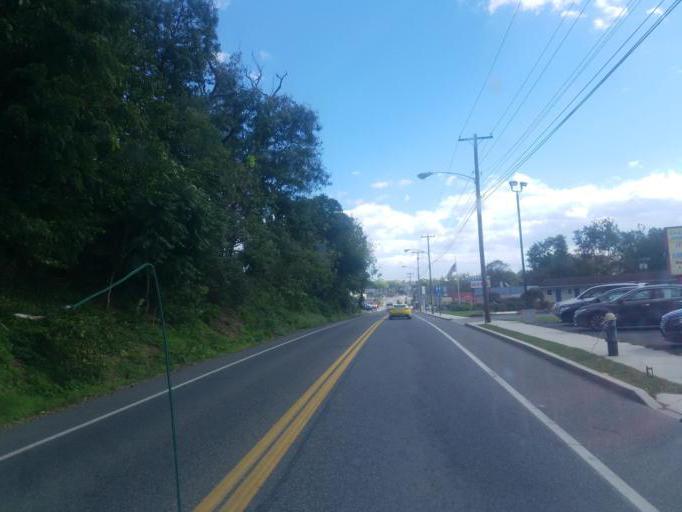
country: US
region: Pennsylvania
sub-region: Franklin County
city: Chambersburg
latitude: 39.9363
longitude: -77.6700
